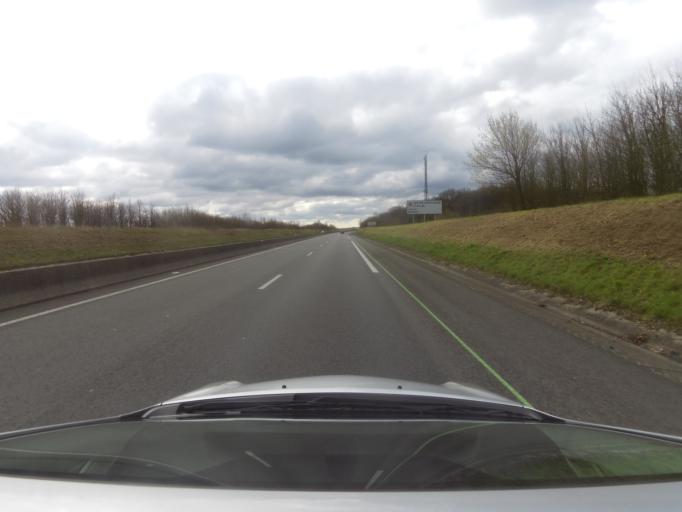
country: FR
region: Nord-Pas-de-Calais
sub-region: Departement du Pas-de-Calais
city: Etaples
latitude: 50.5294
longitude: 1.6839
